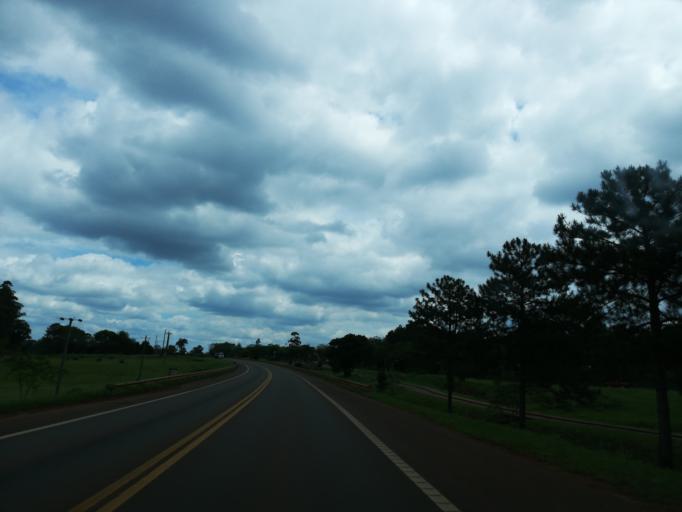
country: AR
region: Misiones
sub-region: Departamento de Leandro N. Alem
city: Leandro N. Alem
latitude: -27.6184
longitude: -55.3313
